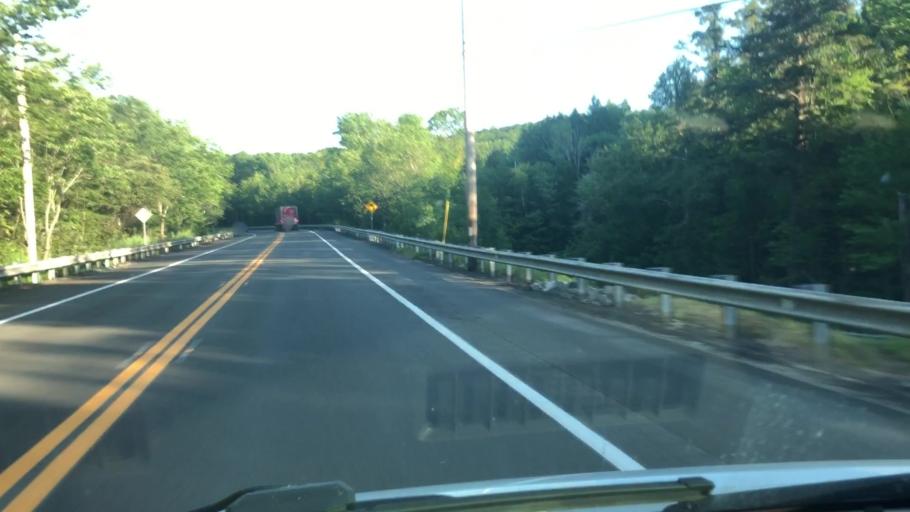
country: US
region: Massachusetts
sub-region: Hampshire County
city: Chesterfield
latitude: 42.4551
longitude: -72.8489
